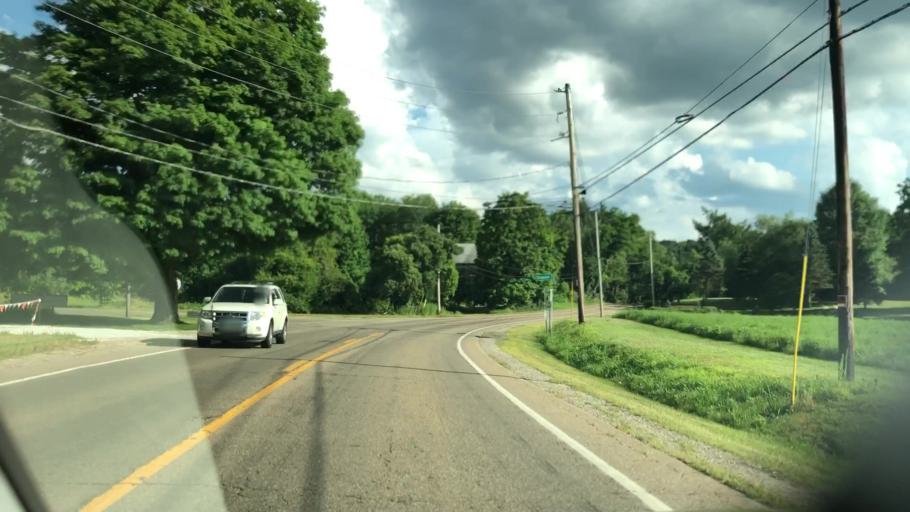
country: US
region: Ohio
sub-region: Summit County
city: Norton
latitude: 41.0748
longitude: -81.6392
